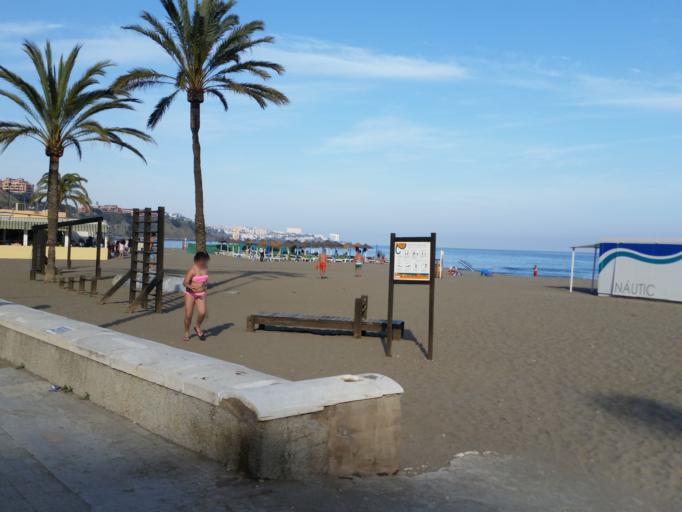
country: ES
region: Andalusia
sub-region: Provincia de Malaga
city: Benalmadena
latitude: 36.5695
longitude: -4.5933
